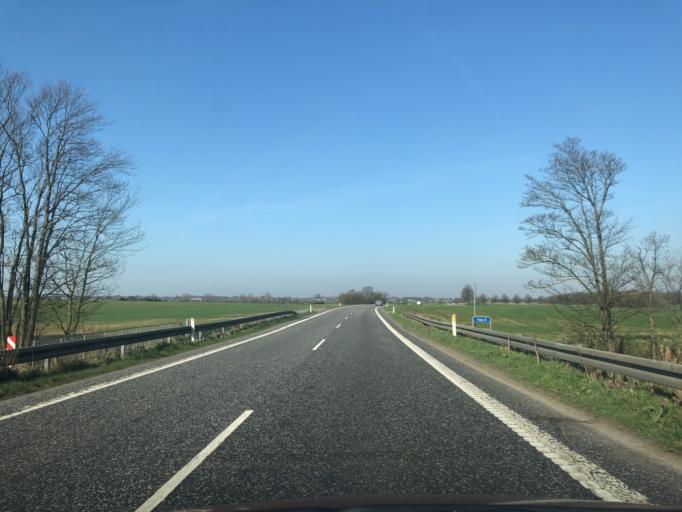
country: DK
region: Zealand
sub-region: Faxe Kommune
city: Fakse
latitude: 55.2557
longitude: 12.0717
